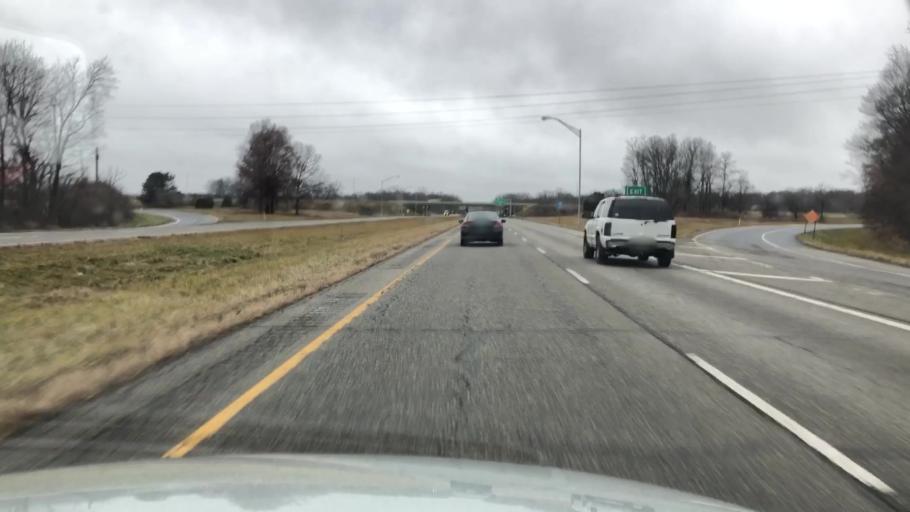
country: US
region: Indiana
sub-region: Marshall County
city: Plymouth
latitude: 41.3473
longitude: -86.2697
